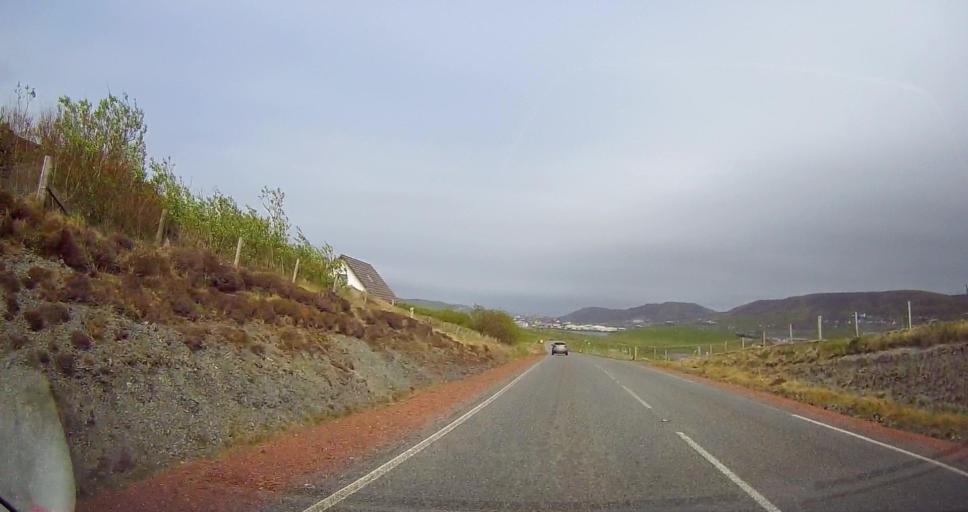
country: GB
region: Scotland
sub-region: Shetland Islands
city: Sandwick
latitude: 60.1215
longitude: -1.2880
